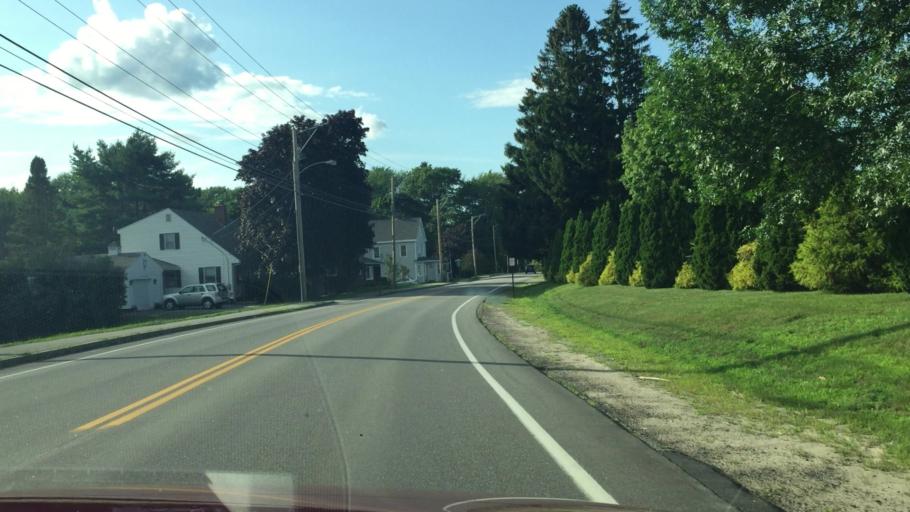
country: US
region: Maine
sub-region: Cumberland County
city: Westbrook
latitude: 43.6670
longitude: -70.3476
